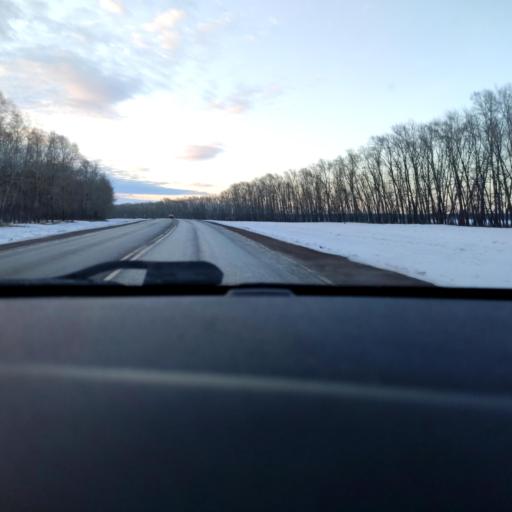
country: RU
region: Bashkortostan
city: Kushnarenkovo
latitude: 55.0933
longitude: 55.3405
